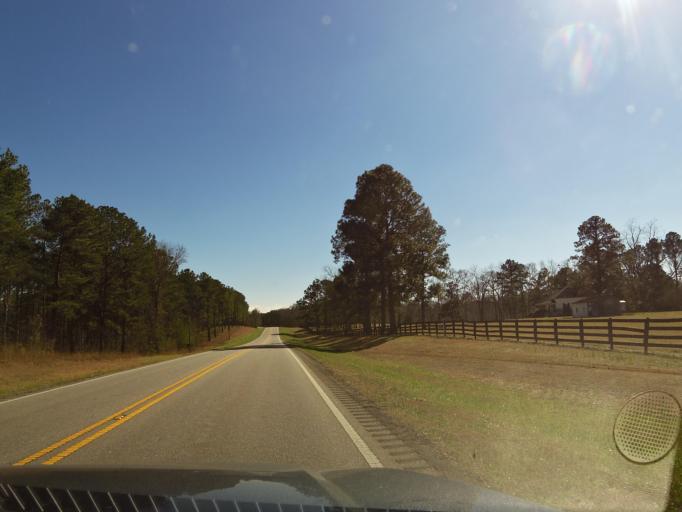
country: US
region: Alabama
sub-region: Bullock County
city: Union Springs
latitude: 32.1160
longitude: -85.5869
